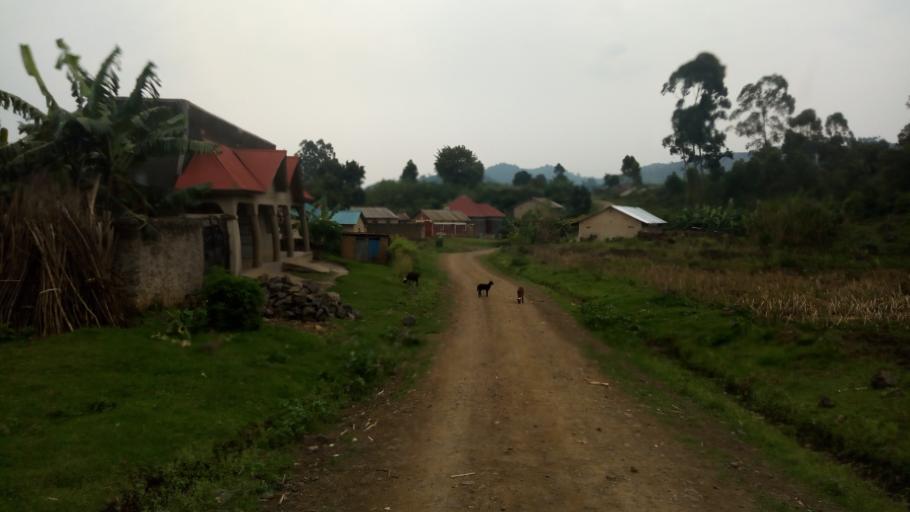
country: UG
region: Western Region
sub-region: Kisoro District
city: Kisoro
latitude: -1.2685
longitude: 29.6254
